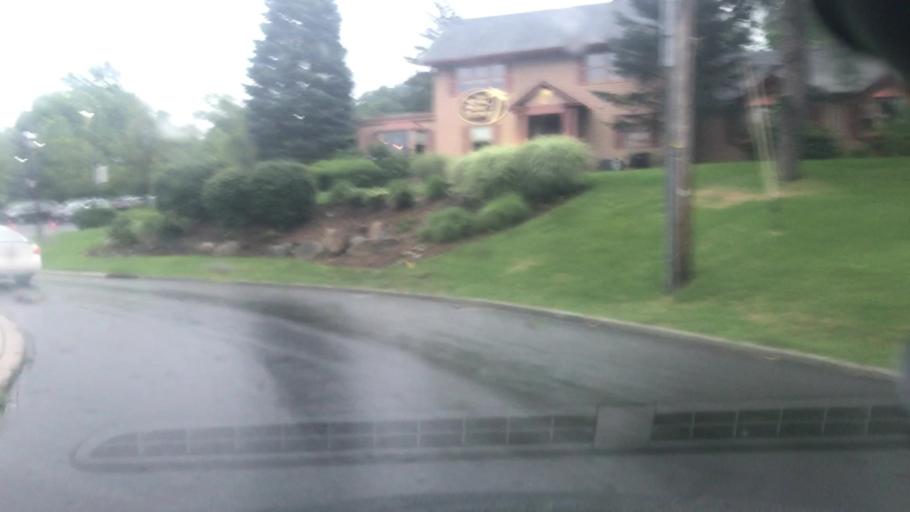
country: US
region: New Jersey
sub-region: Bergen County
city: Mahwah
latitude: 41.0979
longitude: -74.1625
